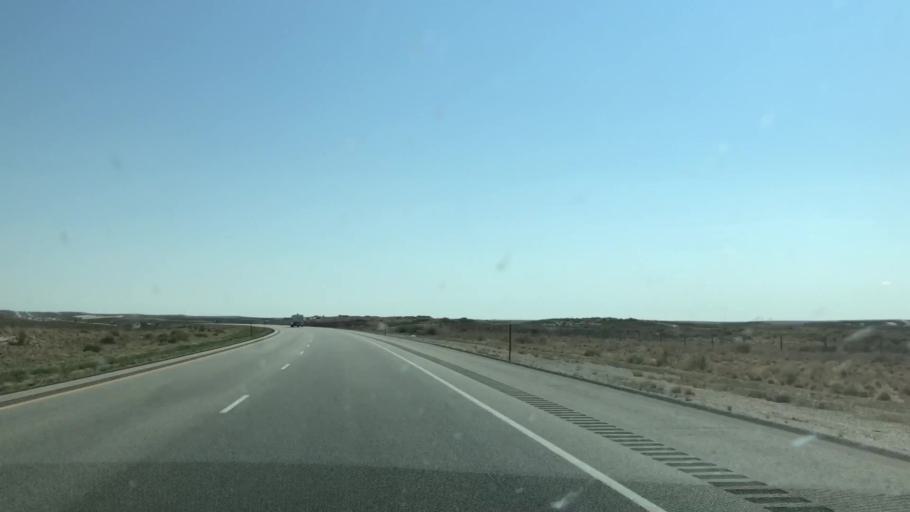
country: US
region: Wyoming
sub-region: Carbon County
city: Rawlins
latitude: 41.7024
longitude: -107.8454
